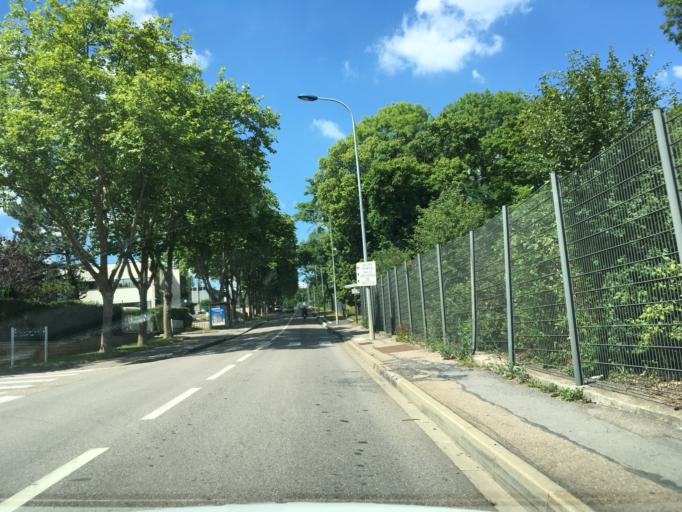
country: FR
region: Lorraine
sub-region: Departement de Meurthe-et-Moselle
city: Laxou
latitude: 48.6965
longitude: 6.1378
